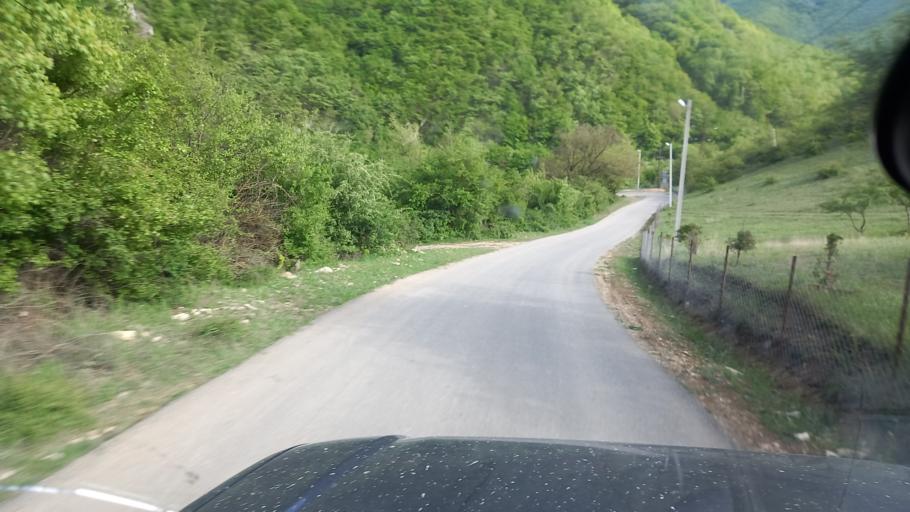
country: RU
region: Dagestan
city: Khuchni
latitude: 41.9661
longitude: 47.9583
